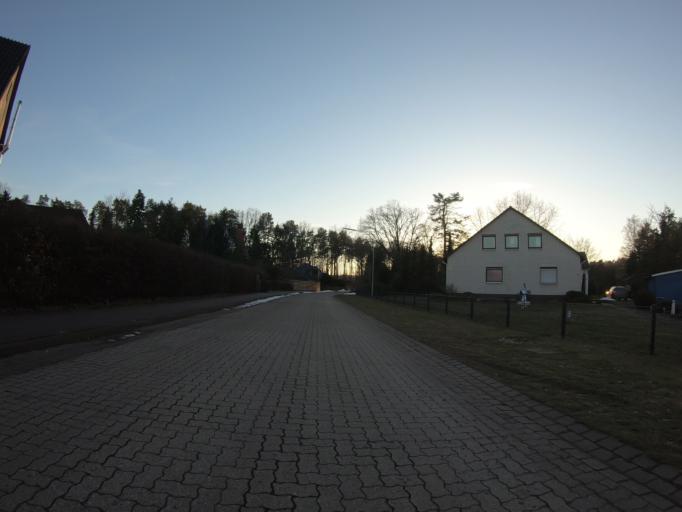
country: DE
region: Lower Saxony
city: Gifhorn
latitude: 52.4746
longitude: 10.5299
